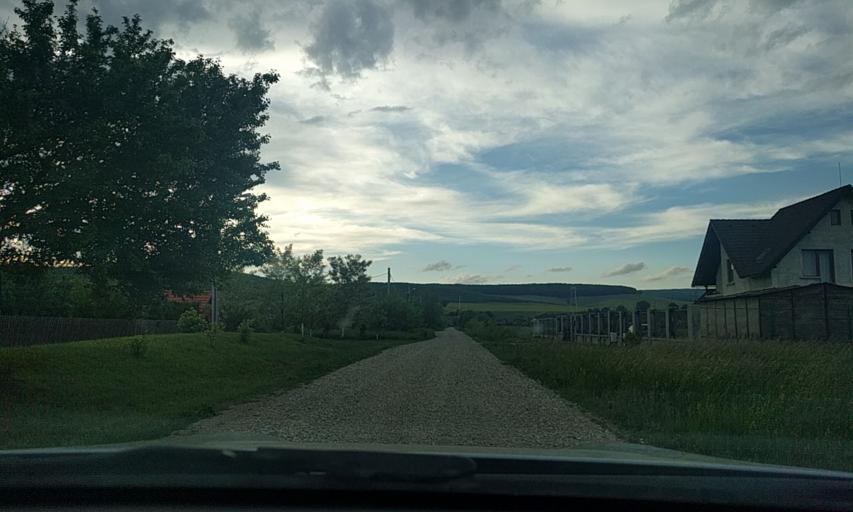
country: RO
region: Covasna
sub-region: Comuna Ilieni
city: Ilieni
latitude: 45.7631
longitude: 25.7206
